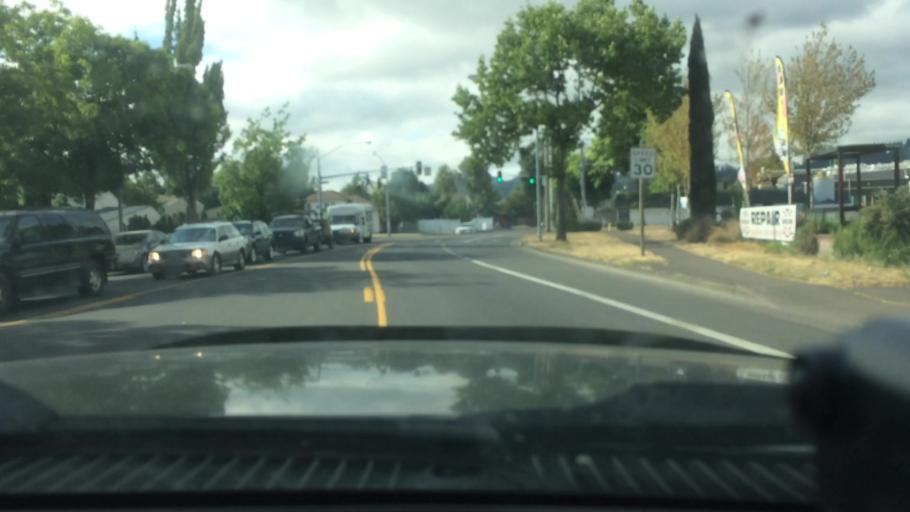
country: US
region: Oregon
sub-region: Lane County
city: Eugene
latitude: 44.0517
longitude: -123.1184
